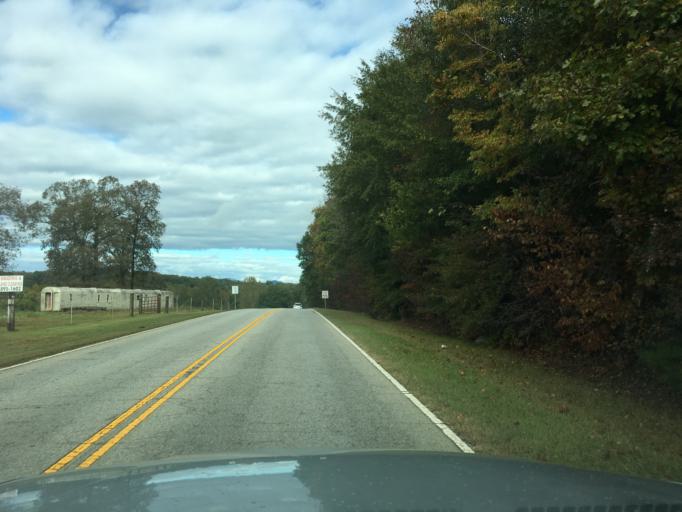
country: US
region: South Carolina
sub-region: Greenville County
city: Greer
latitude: 35.0130
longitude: -82.2600
